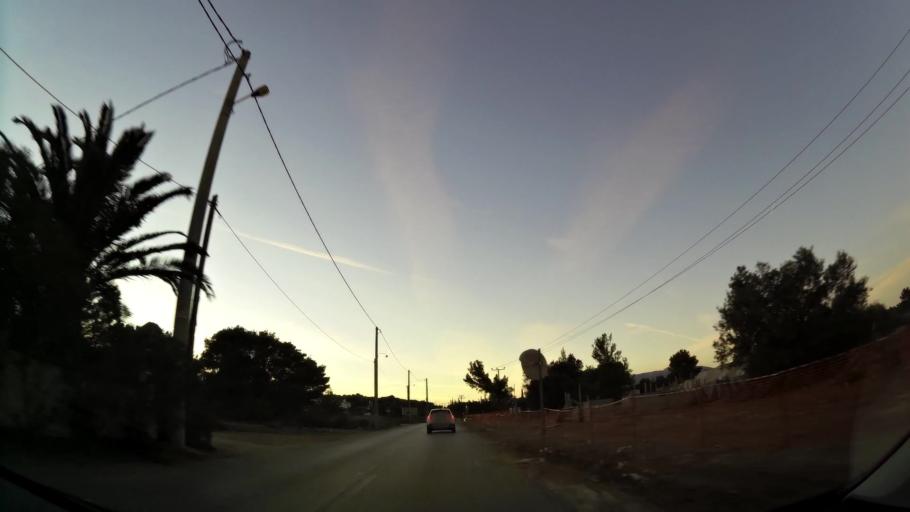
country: GR
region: Attica
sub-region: Nomarchia Anatolikis Attikis
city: Rafina
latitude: 38.0017
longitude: 23.9880
